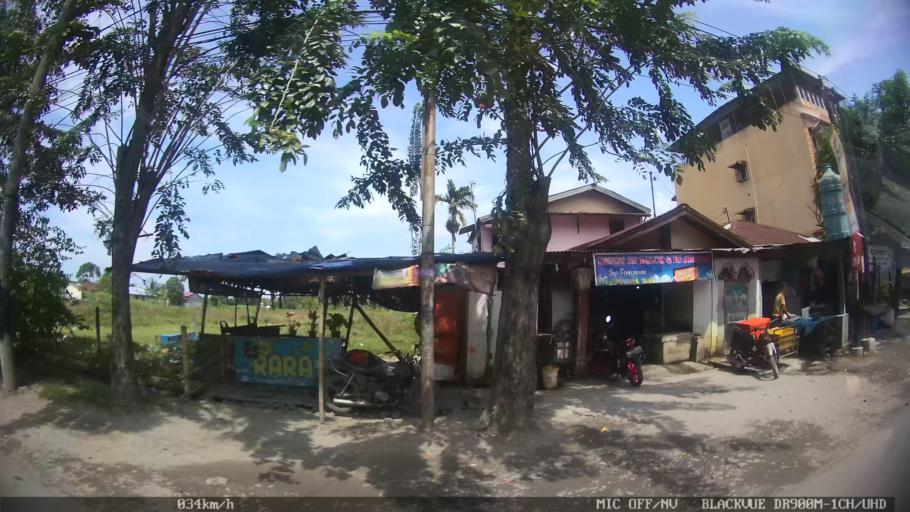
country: ID
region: North Sumatra
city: Labuhan Deli
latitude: 3.6810
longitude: 98.6561
